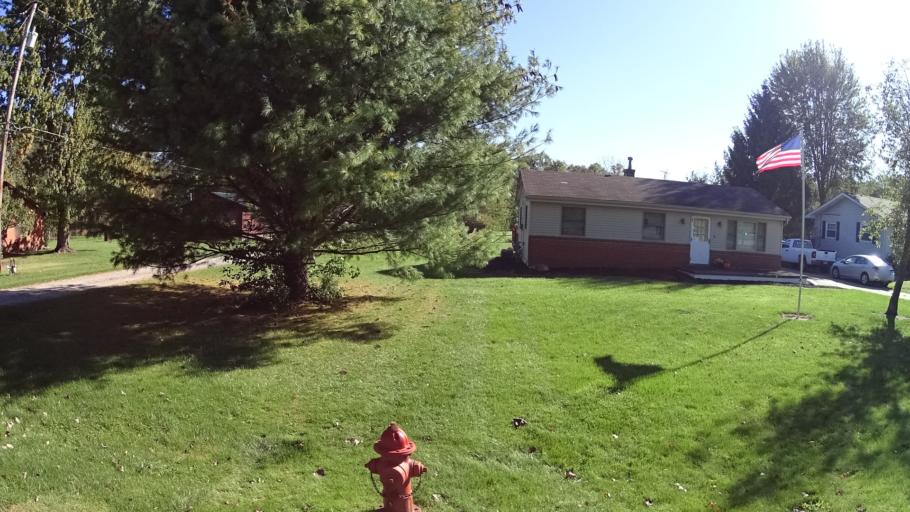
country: US
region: Ohio
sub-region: Lorain County
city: South Amherst
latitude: 41.3476
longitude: -82.2301
